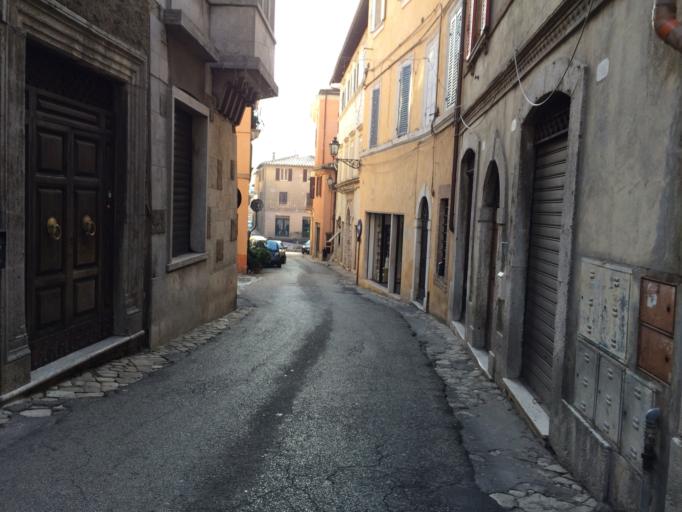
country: IT
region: Umbria
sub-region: Provincia di Terni
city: Amelia
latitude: 42.5553
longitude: 12.4153
